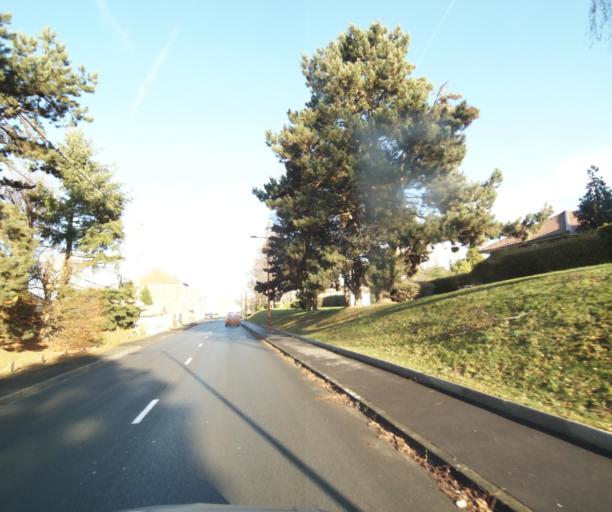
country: FR
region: Nord-Pas-de-Calais
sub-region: Departement du Nord
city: Valenciennes
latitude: 50.3434
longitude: 3.5309
